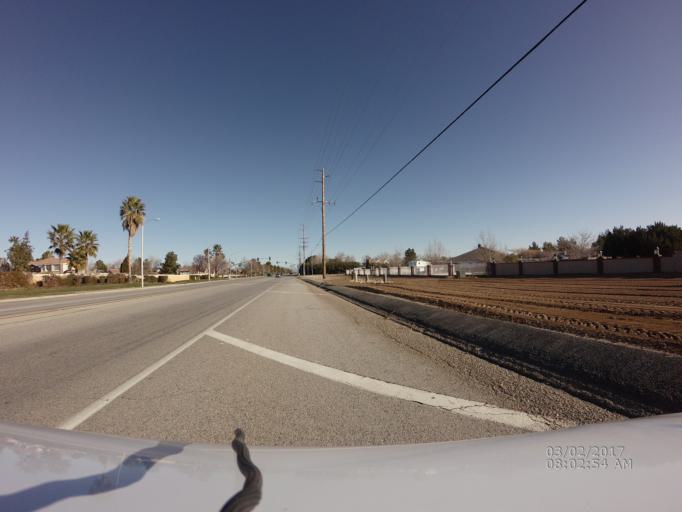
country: US
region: California
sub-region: Los Angeles County
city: Desert View Highlands
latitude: 34.6153
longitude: -118.1836
